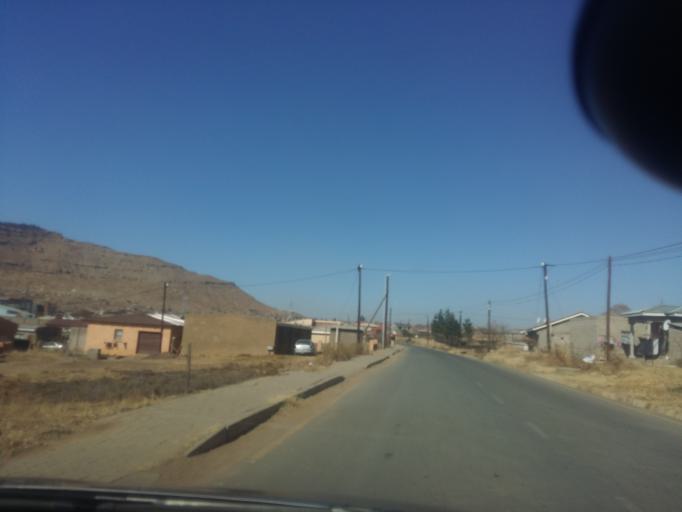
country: LS
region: Maseru
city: Maseru
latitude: -29.3407
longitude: 27.4540
